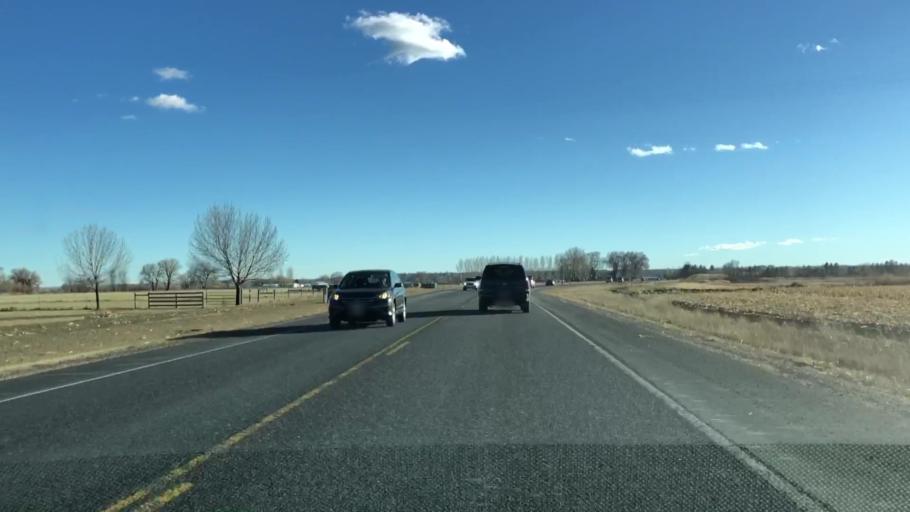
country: US
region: Colorado
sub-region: Weld County
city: Windsor
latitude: 40.5141
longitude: -104.9821
